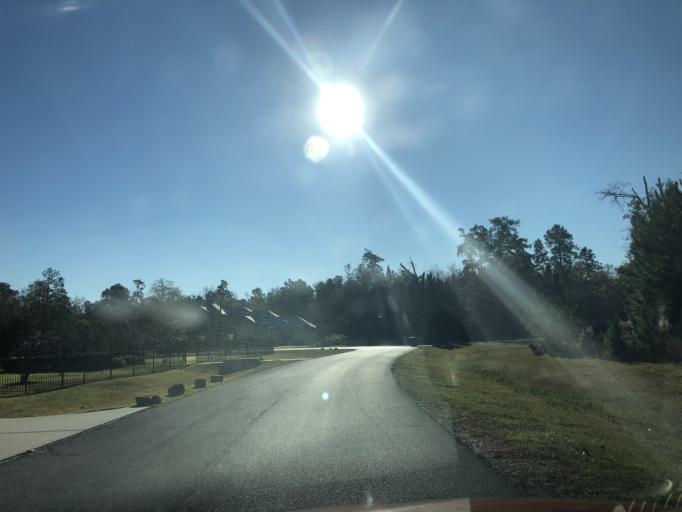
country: US
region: Texas
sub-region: Montgomery County
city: Porter Heights
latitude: 30.0684
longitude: -95.3221
